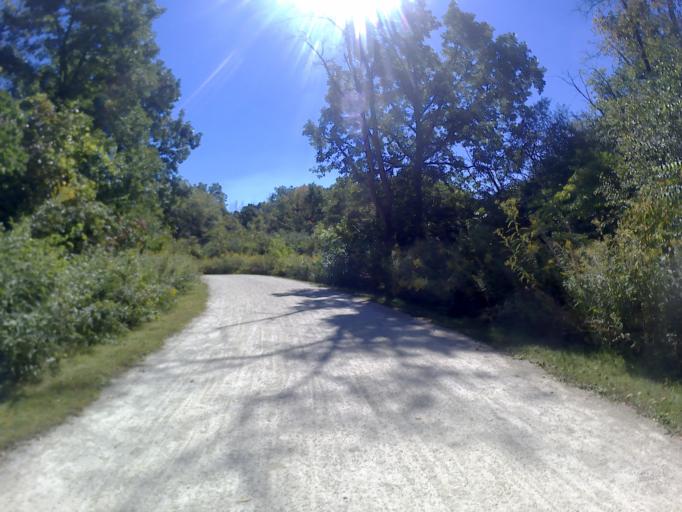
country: US
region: Illinois
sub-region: DuPage County
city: Warrenville
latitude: 41.7875
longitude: -88.1790
